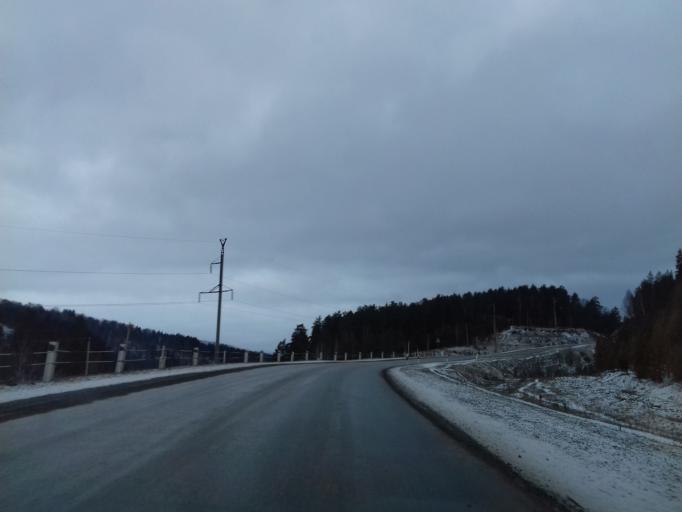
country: RU
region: Bashkortostan
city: Starosubkhangulovo
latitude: 53.1258
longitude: 57.4165
